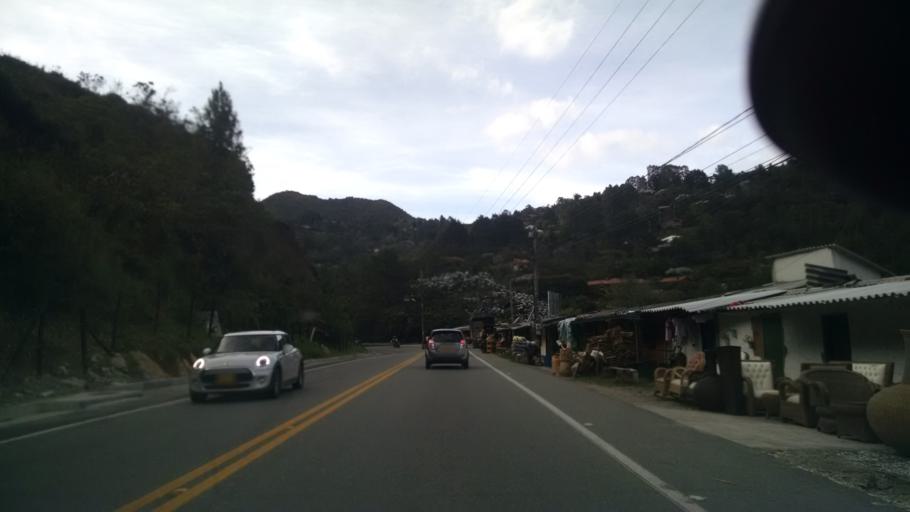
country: CO
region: Antioquia
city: El Retiro
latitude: 6.1280
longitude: -75.5014
